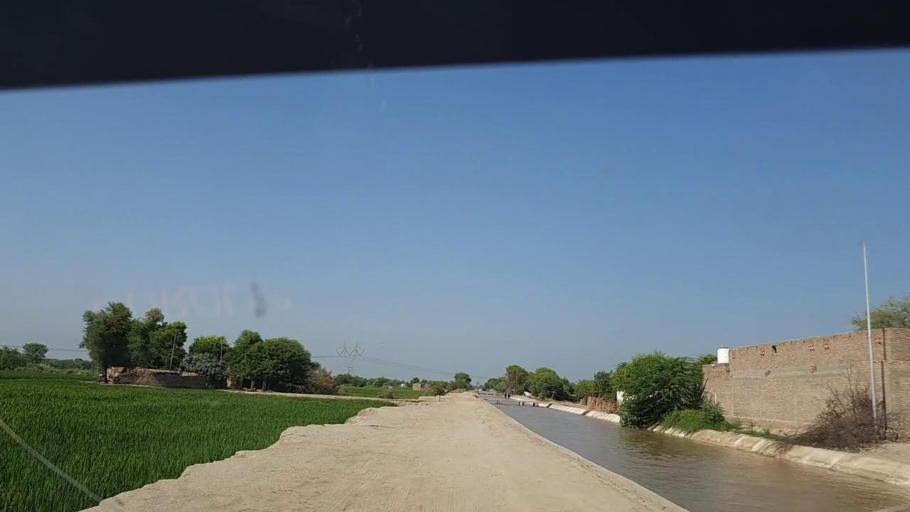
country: PK
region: Sindh
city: Ghauspur
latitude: 28.1650
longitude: 69.0958
